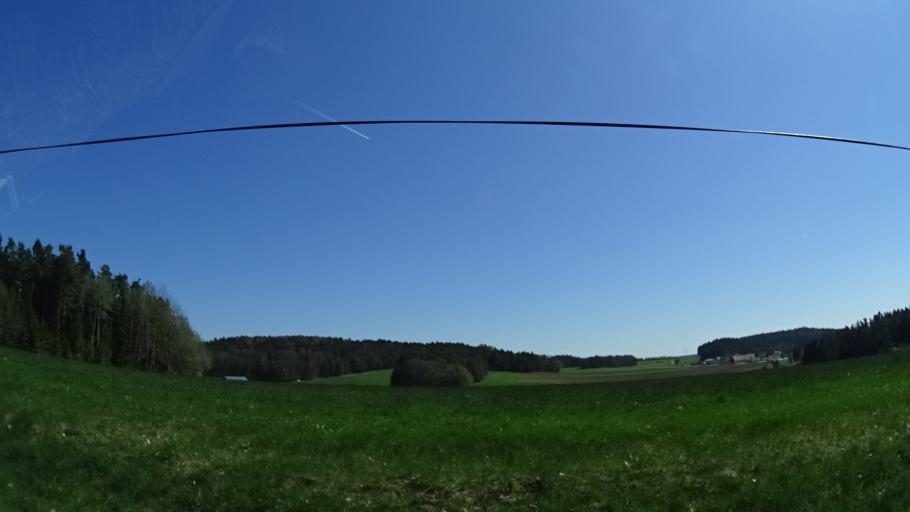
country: DE
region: Bavaria
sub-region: Upper Palatinate
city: Kastl
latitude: 49.3922
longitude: 11.7001
